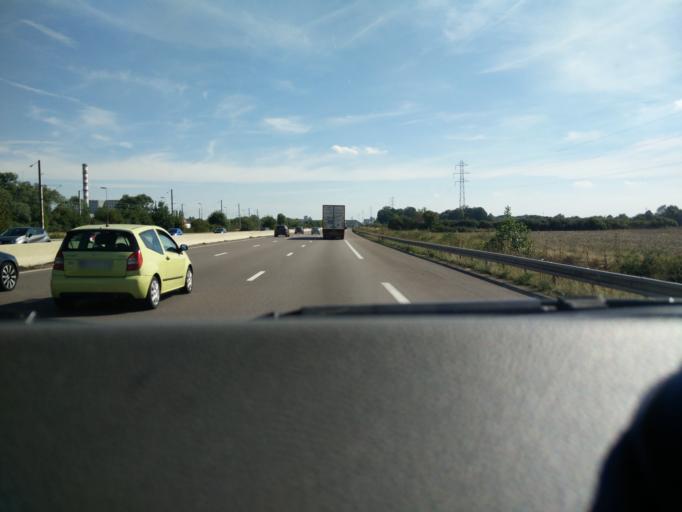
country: FR
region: Lorraine
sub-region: Departement de la Moselle
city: Argancy
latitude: 49.1675
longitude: 6.1808
